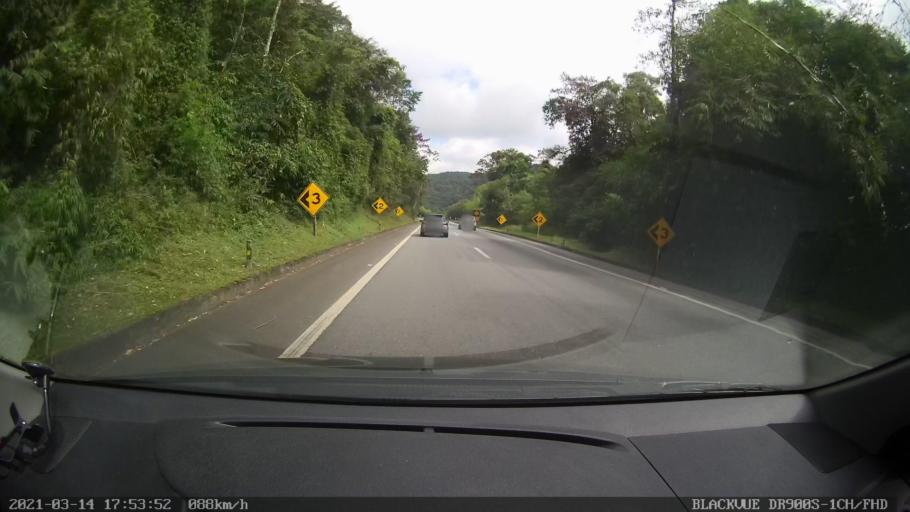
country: BR
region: Rio de Janeiro
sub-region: Petropolis
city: Petropolis
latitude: -22.4833
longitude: -43.2313
